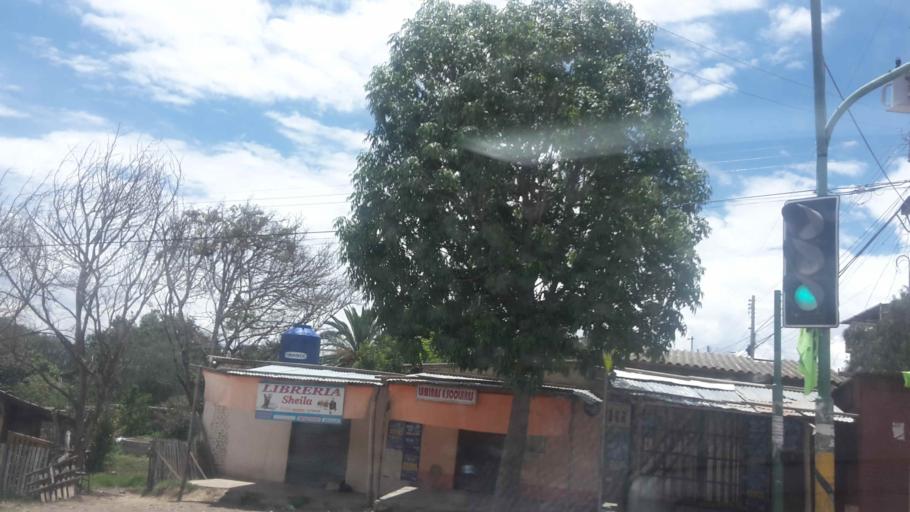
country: BO
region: Cochabamba
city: Cochabamba
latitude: -17.3425
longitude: -66.1788
